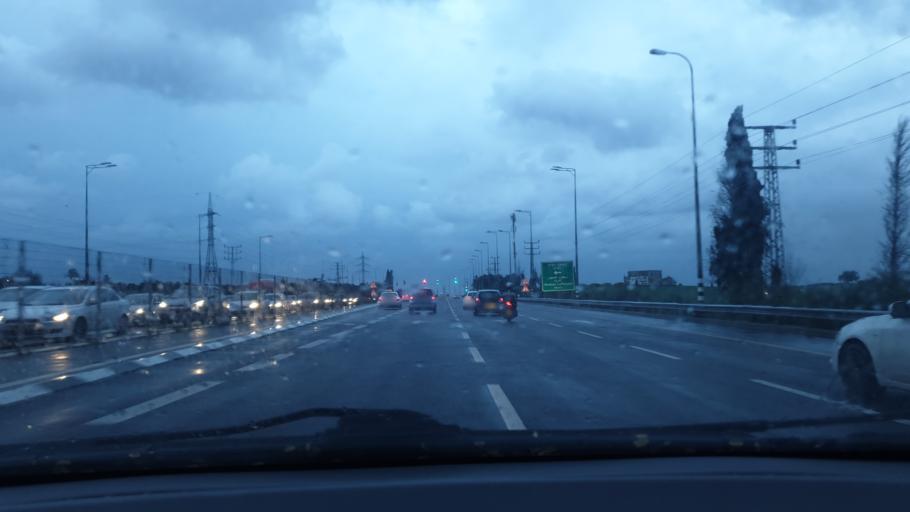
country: IL
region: Central District
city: Kefar Habad
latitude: 31.9716
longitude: 34.8420
